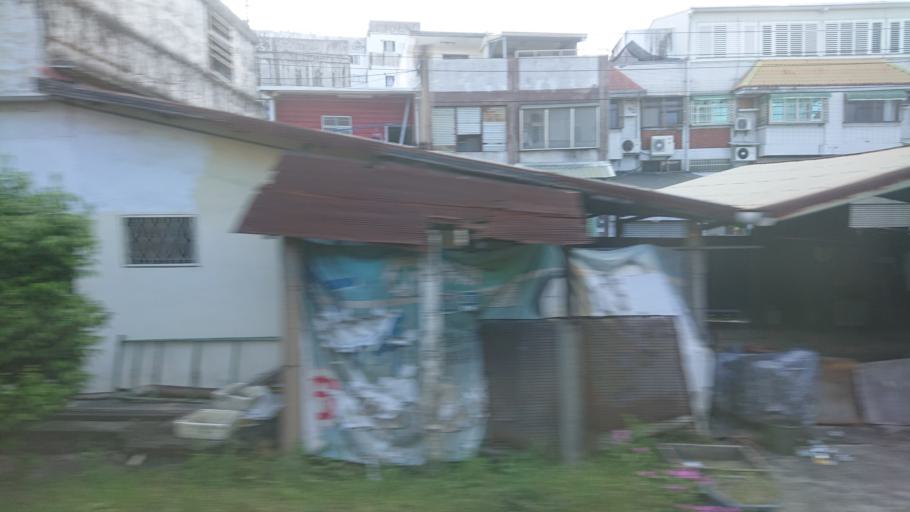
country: TW
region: Taiwan
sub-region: Hualien
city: Hualian
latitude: 23.9850
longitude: 121.5970
